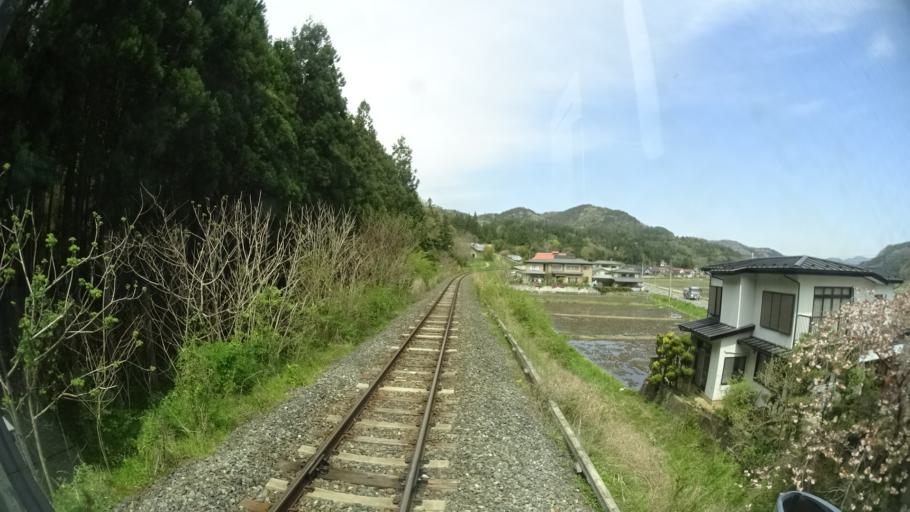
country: JP
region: Iwate
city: Ichinoseki
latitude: 38.9608
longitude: 141.2426
